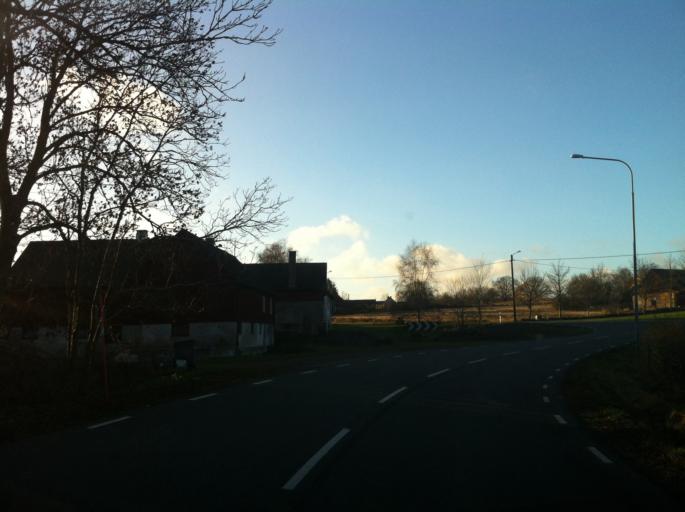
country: SE
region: Skane
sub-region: Ostra Goinge Kommun
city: Knislinge
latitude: 56.1826
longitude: 13.9894
